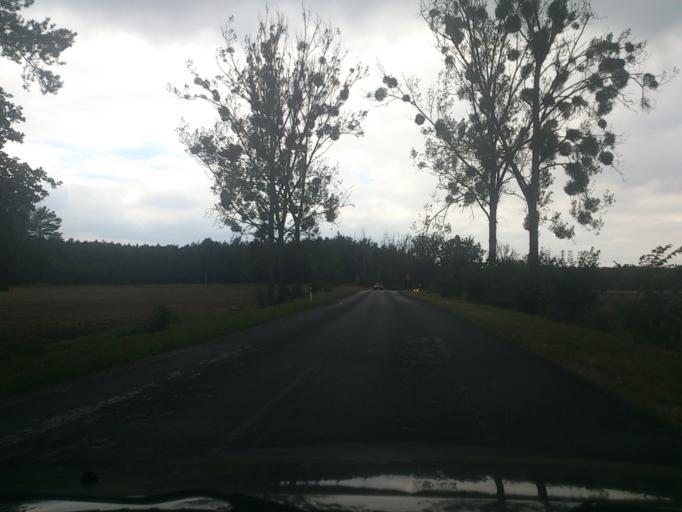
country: PL
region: Kujawsko-Pomorskie
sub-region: Powiat golubsko-dobrzynski
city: Golub-Dobrzyn
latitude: 53.0882
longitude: 19.0531
